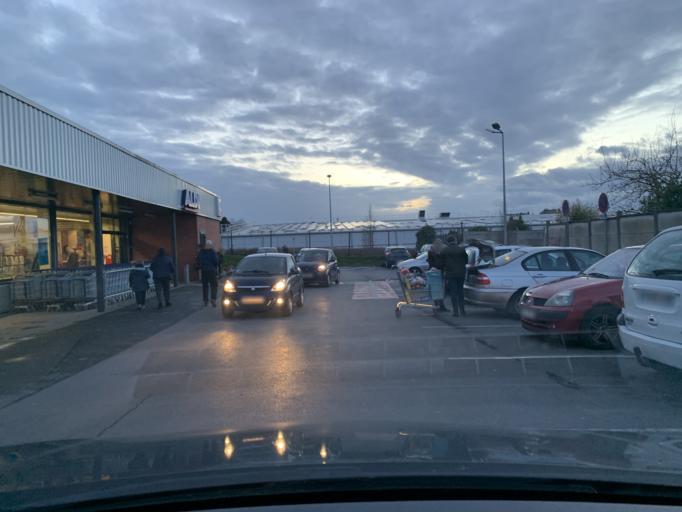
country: FR
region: Nord-Pas-de-Calais
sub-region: Departement du Nord
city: Cambrai
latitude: 50.1809
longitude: 3.2496
